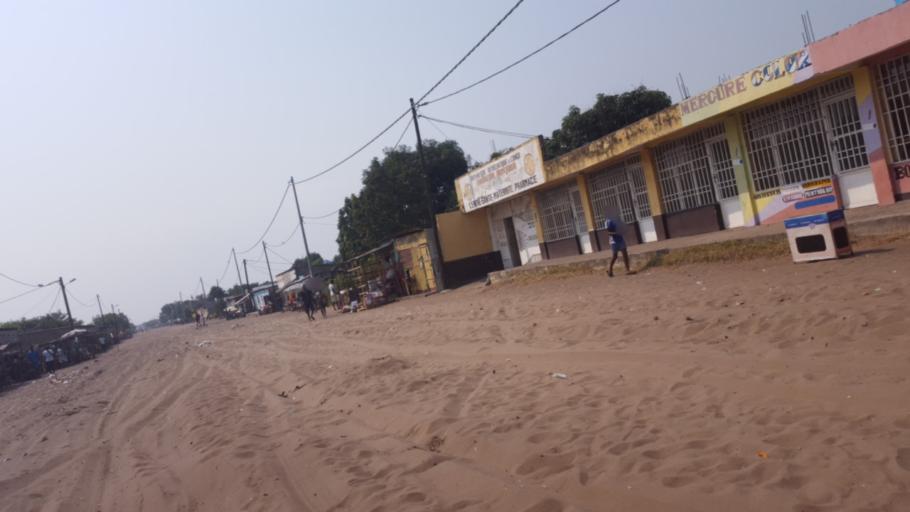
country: CD
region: Kinshasa
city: Masina
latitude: -4.3679
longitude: 15.5141
